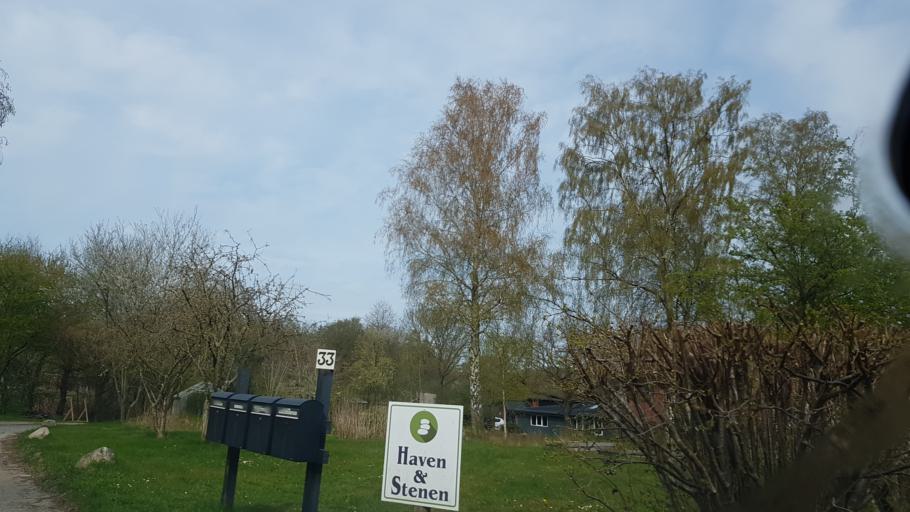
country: DK
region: Capital Region
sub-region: Allerod Kommune
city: Lillerod
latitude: 55.8652
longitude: 12.3650
